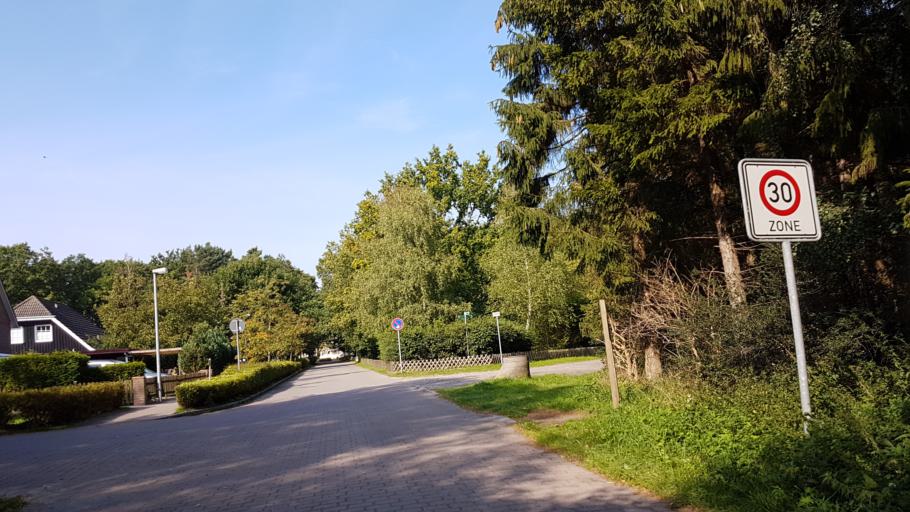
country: DE
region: Mecklenburg-Vorpommern
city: Glowe
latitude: 54.5663
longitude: 13.4592
